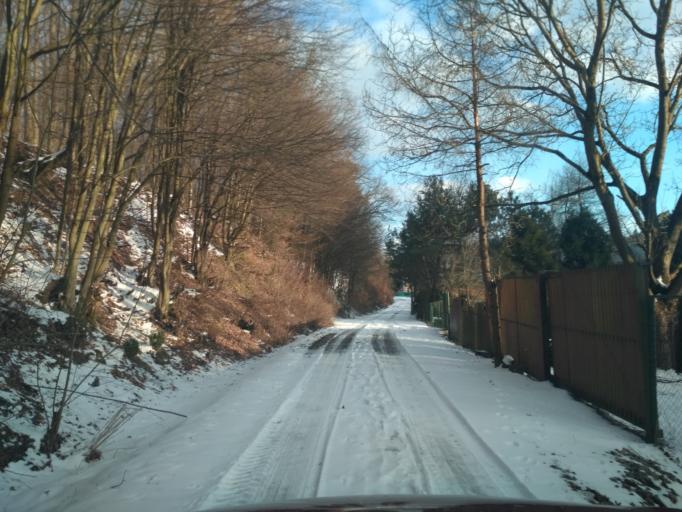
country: SK
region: Kosicky
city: Kosice
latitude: 48.7366
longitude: 21.1569
